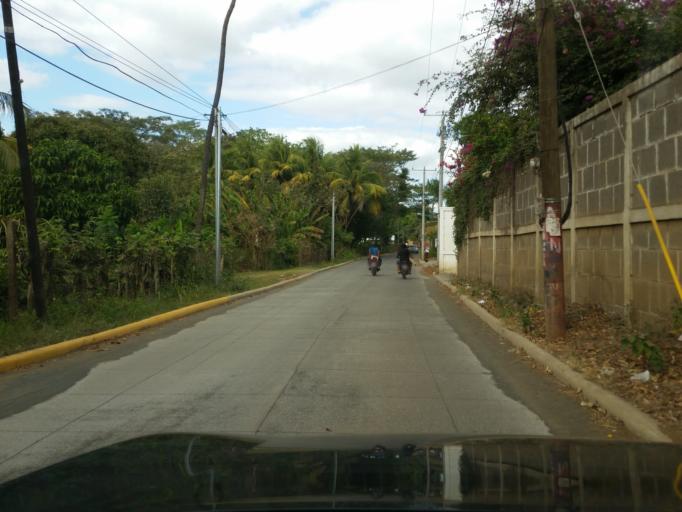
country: NI
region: Masaya
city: Ticuantepe
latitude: 12.0770
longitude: -86.2286
